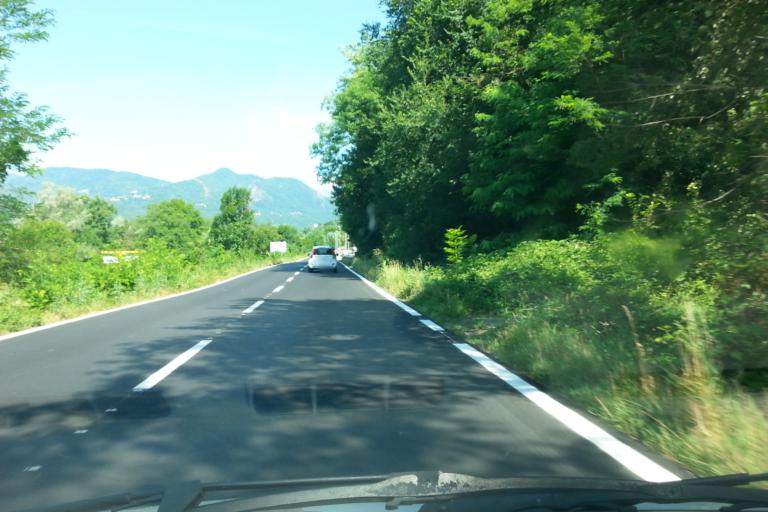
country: IT
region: Piedmont
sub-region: Provincia di Torino
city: Trana
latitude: 45.0470
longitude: 7.4064
